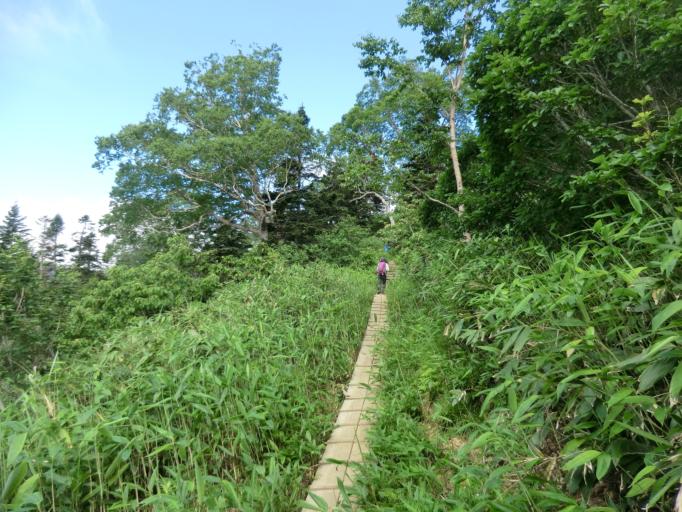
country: JP
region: Gunma
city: Numata
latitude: 36.8835
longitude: 139.1842
